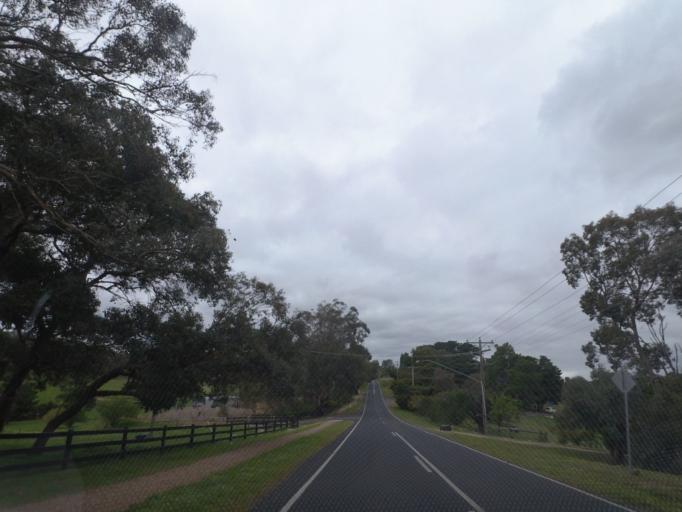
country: AU
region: Victoria
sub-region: Nillumbik
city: Hurstbridge
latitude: -37.6438
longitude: 145.2226
